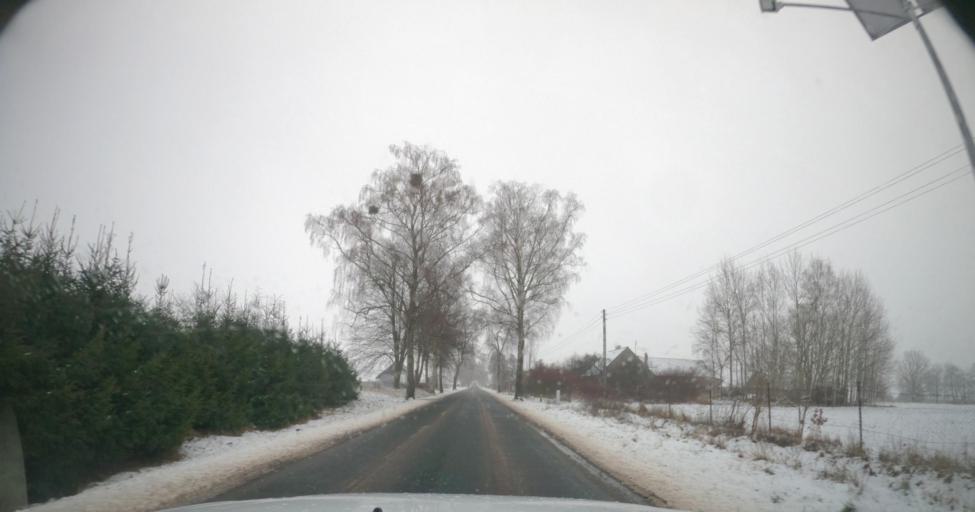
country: PL
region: West Pomeranian Voivodeship
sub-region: Powiat gryficki
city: Gryfice
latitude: 53.9059
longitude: 15.2744
